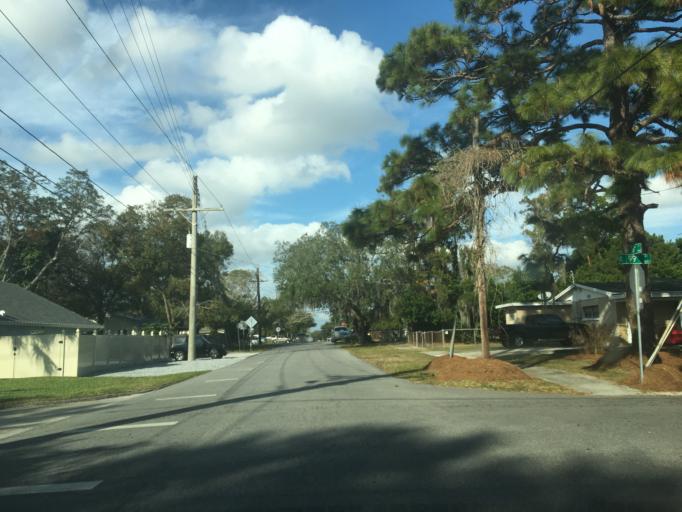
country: US
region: Florida
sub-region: Hillsborough County
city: University
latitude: 28.0391
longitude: -82.4305
